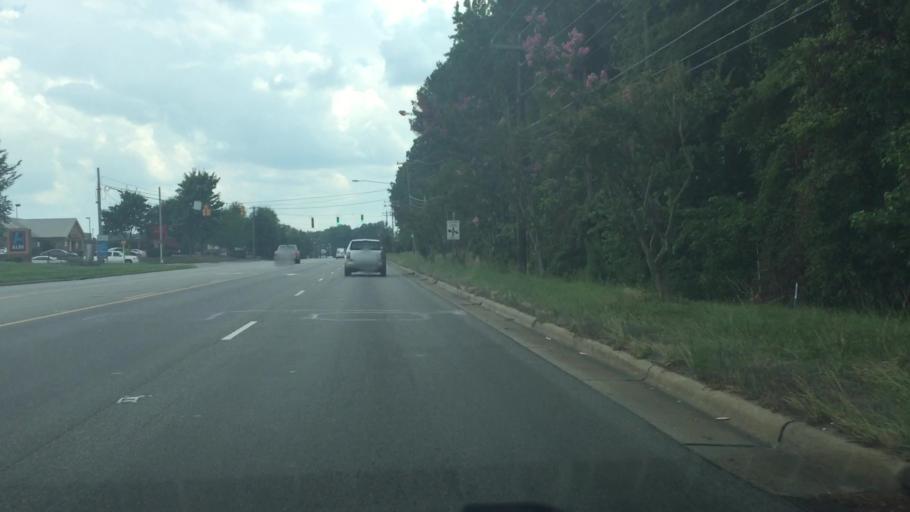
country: US
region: North Carolina
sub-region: Rowan County
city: Salisbury
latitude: 35.6696
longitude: -80.4996
